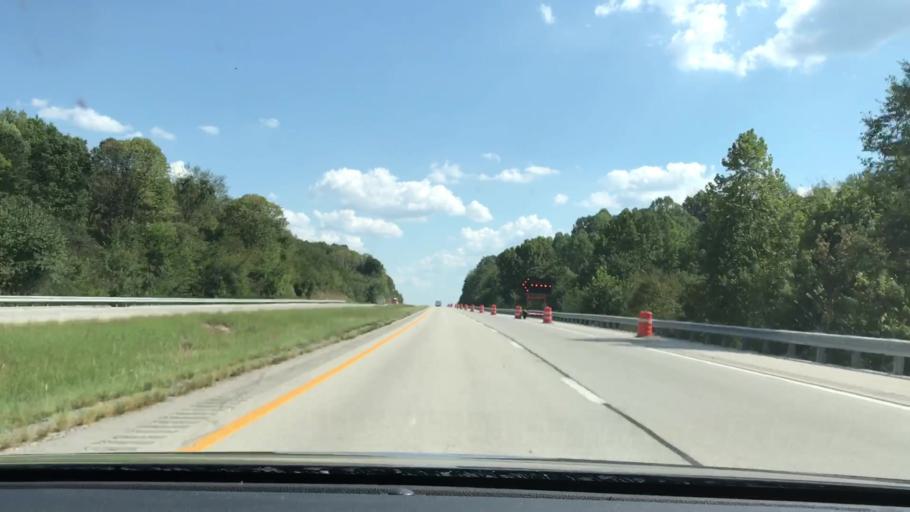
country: US
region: Kentucky
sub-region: Butler County
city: Morgantown
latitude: 37.2294
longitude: -86.7249
